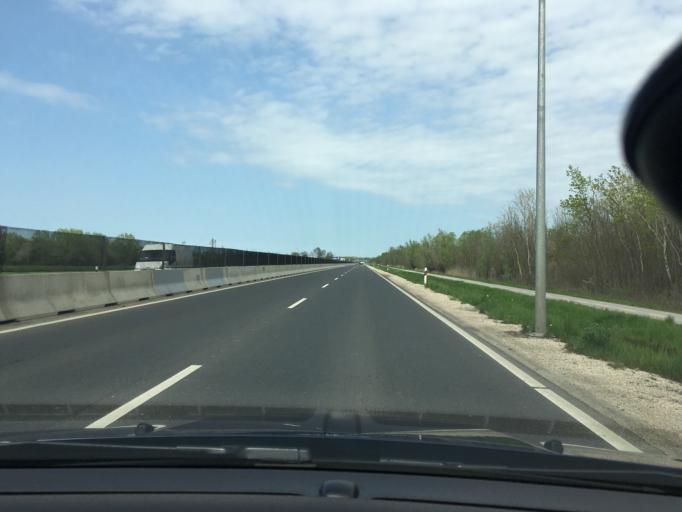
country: HU
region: Csongrad
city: Algyo
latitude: 46.3248
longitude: 20.1944
